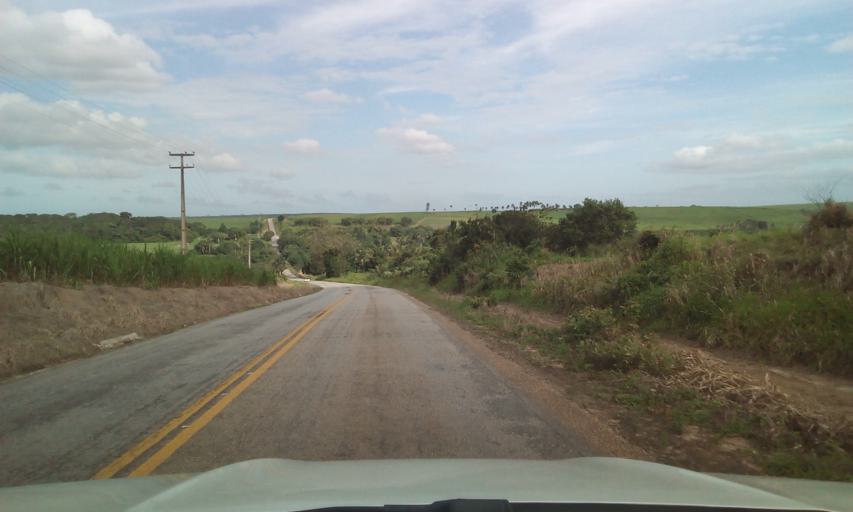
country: BR
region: Paraiba
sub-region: Santa Rita
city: Santa Rita
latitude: -6.9947
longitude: -34.9891
